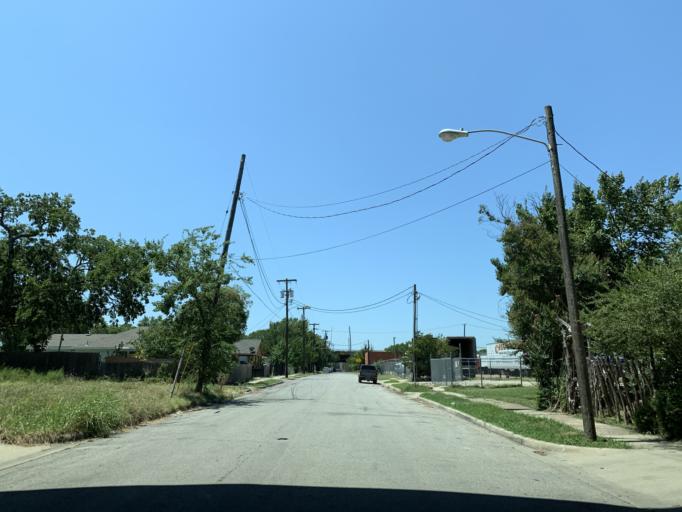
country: US
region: Texas
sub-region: Dallas County
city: Dallas
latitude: 32.7763
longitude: -96.7762
